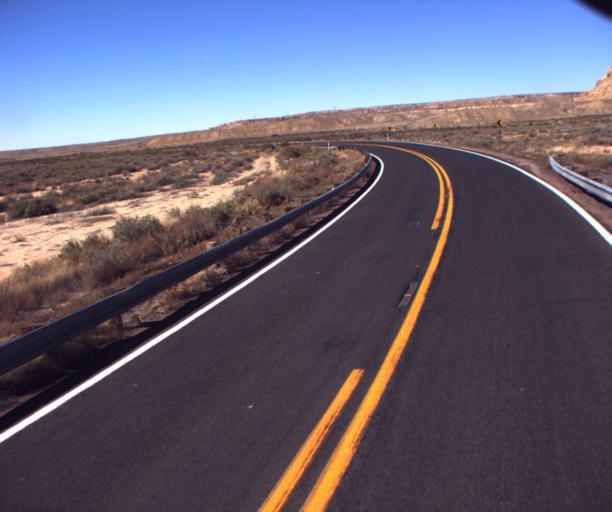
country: US
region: Arizona
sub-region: Navajo County
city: First Mesa
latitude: 35.9836
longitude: -110.7079
